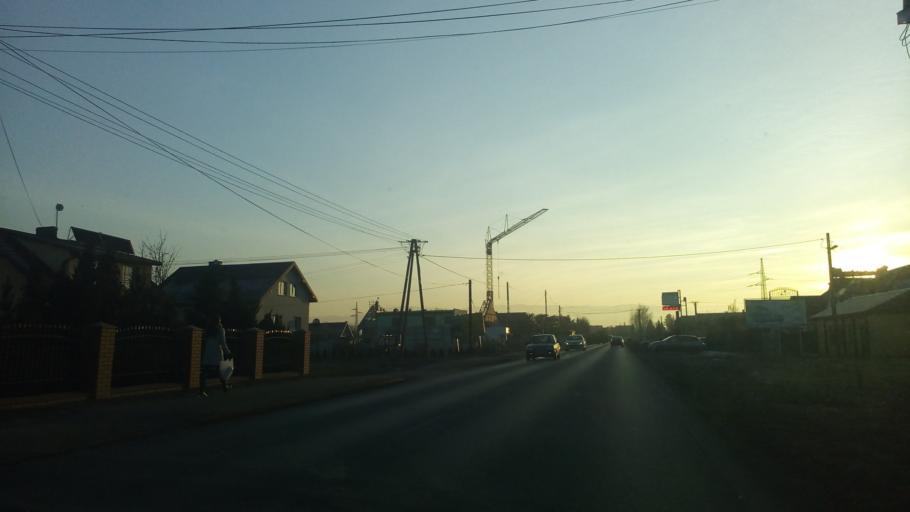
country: PL
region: Lesser Poland Voivodeship
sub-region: Powiat nowosadecki
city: Chelmiec
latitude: 49.6142
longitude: 20.6627
